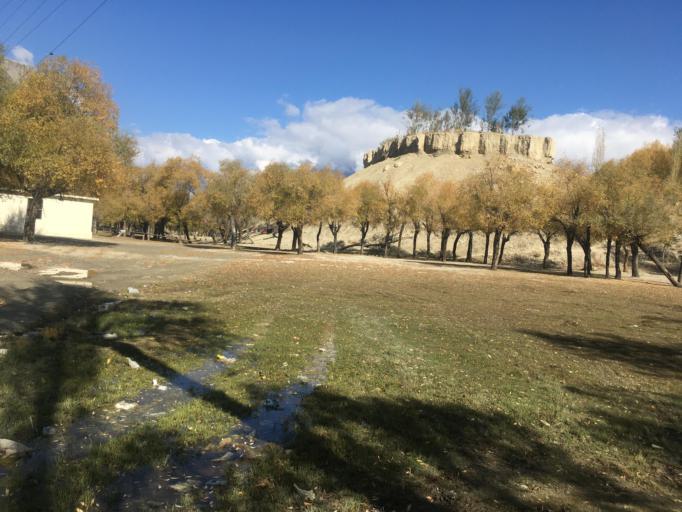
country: PK
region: Gilgit-Baltistan
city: Skardu
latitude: 35.3319
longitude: 75.5214
